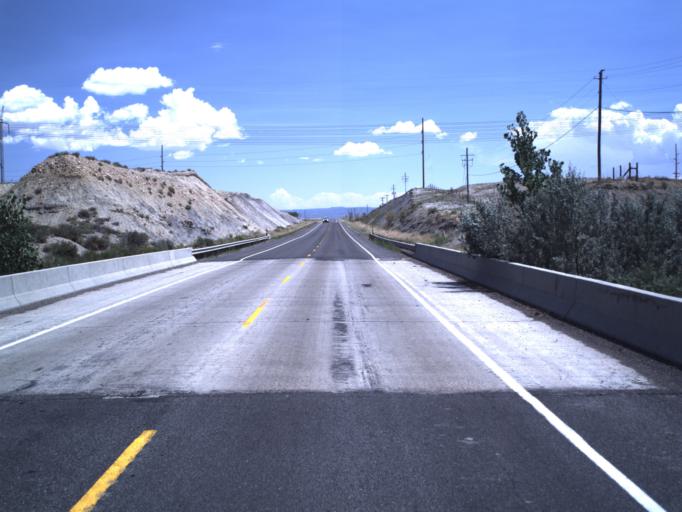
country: US
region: Utah
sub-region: Emery County
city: Huntington
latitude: 39.3466
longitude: -110.9920
